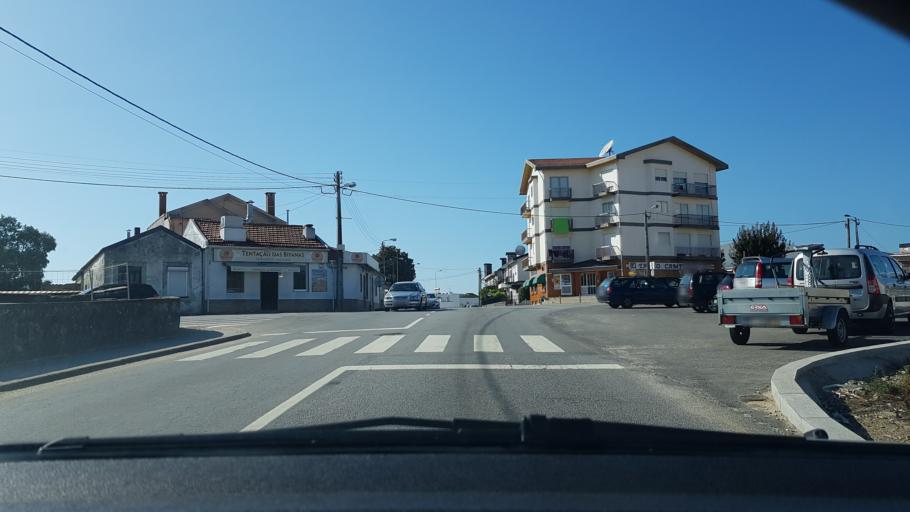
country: PT
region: Porto
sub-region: Gondomar
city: Baguim do Monte
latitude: 41.1839
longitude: -8.5388
